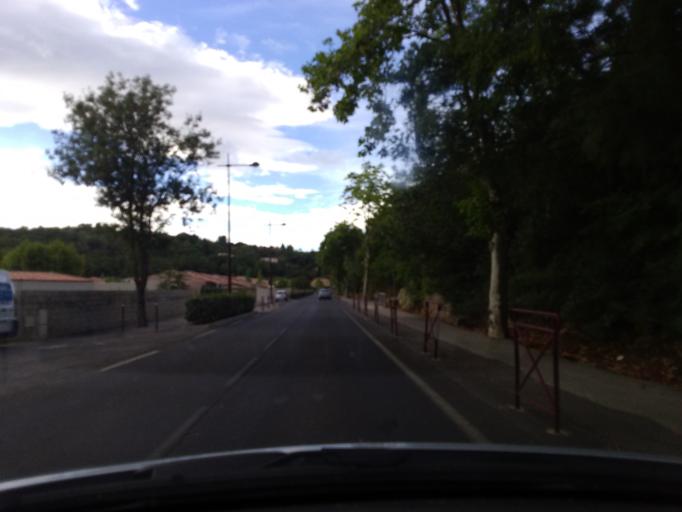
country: FR
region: Languedoc-Roussillon
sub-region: Departement de l'Herault
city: Nebian
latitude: 43.6302
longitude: 3.4189
